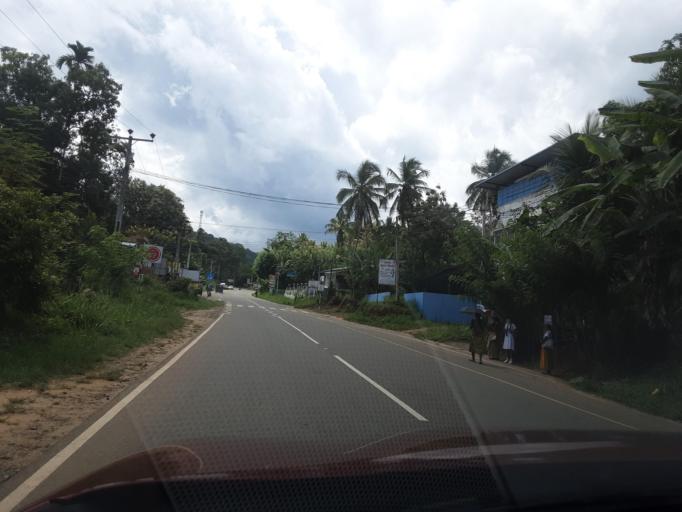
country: LK
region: Uva
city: Monaragala
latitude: 6.8979
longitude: 81.2419
